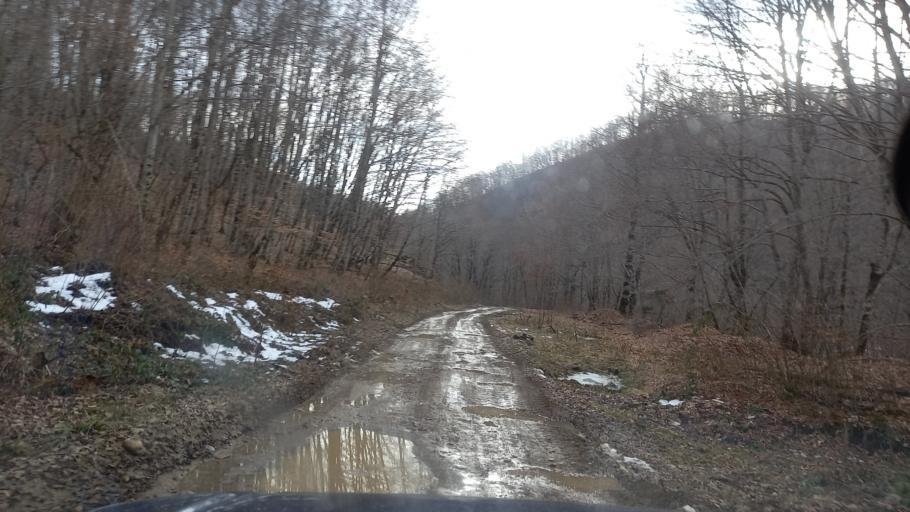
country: RU
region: Adygeya
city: Kamennomostskiy
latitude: 44.1613
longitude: 40.2979
